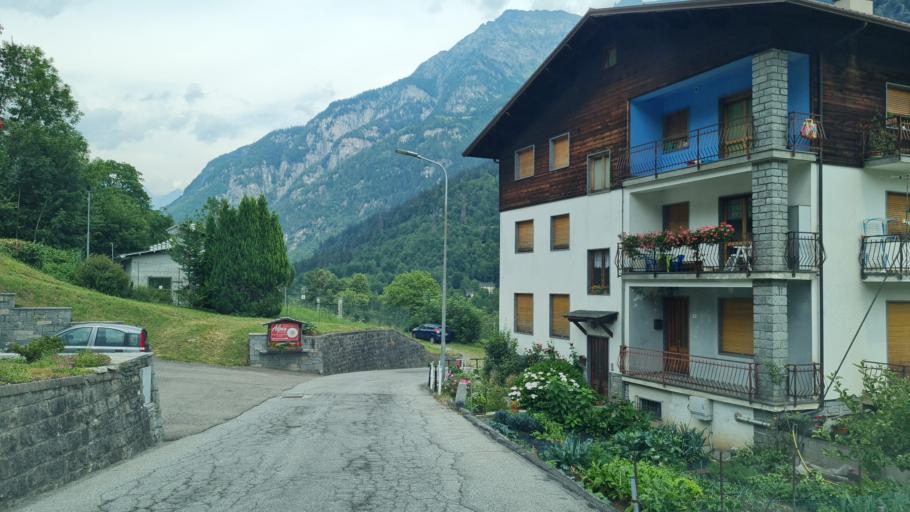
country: IT
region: Piedmont
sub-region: Provincia Verbano-Cusio-Ossola
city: Premia
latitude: 46.2681
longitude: 8.3428
